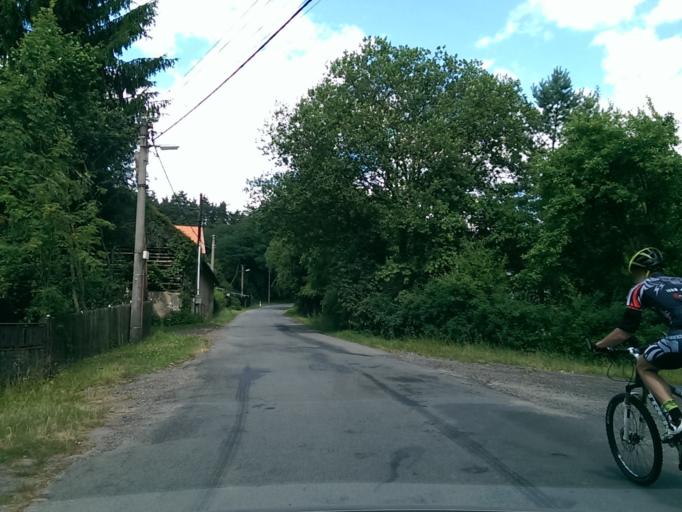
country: CZ
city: Duba
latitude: 50.4913
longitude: 14.5574
